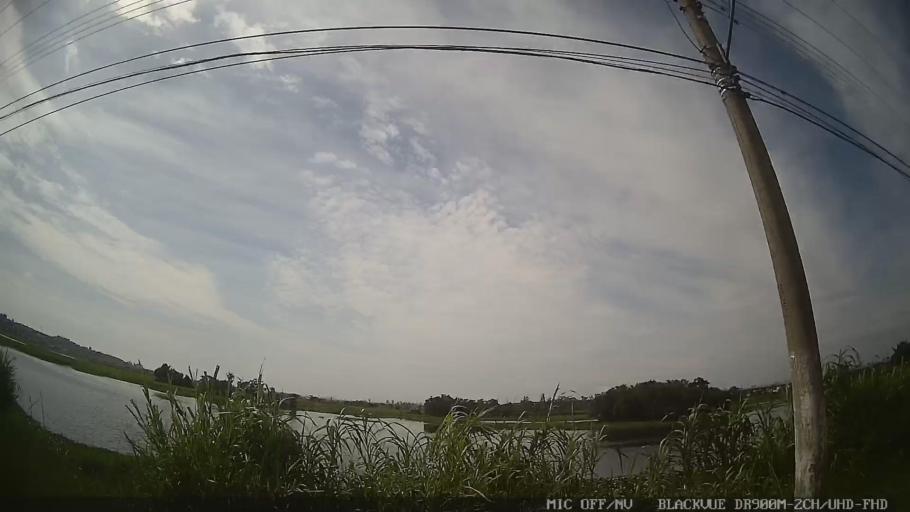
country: BR
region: Sao Paulo
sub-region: Itaquaquecetuba
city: Itaquaquecetuba
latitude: -23.4986
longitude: -46.3321
